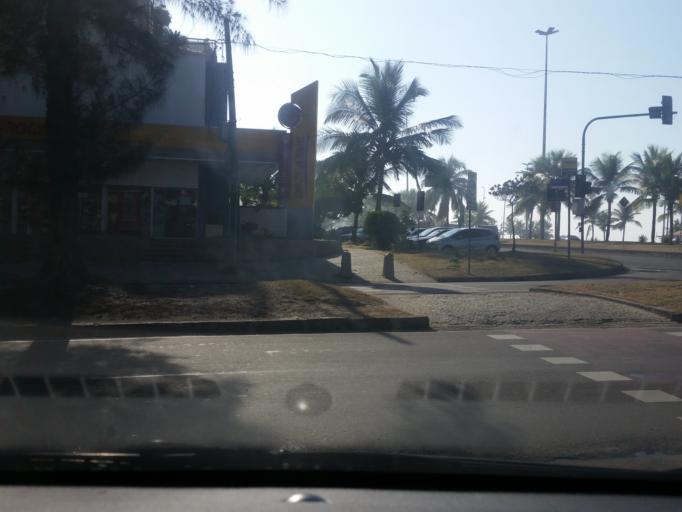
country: BR
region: Rio de Janeiro
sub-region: Nilopolis
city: Nilopolis
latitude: -23.0247
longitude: -43.4574
